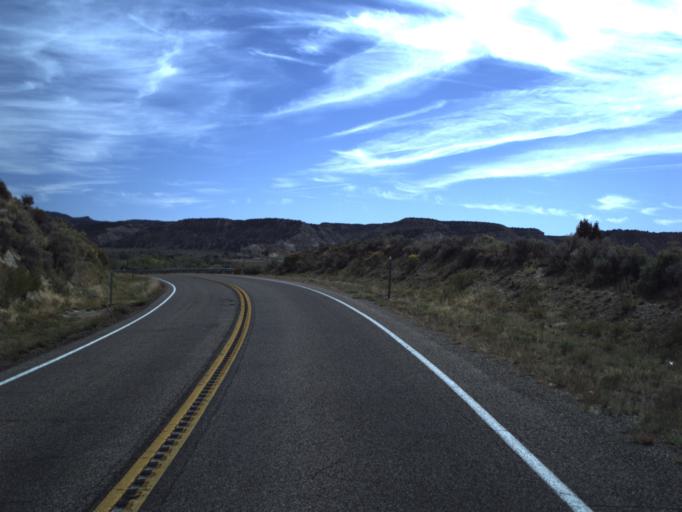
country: US
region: Utah
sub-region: Garfield County
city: Panguitch
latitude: 37.5589
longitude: -112.0207
